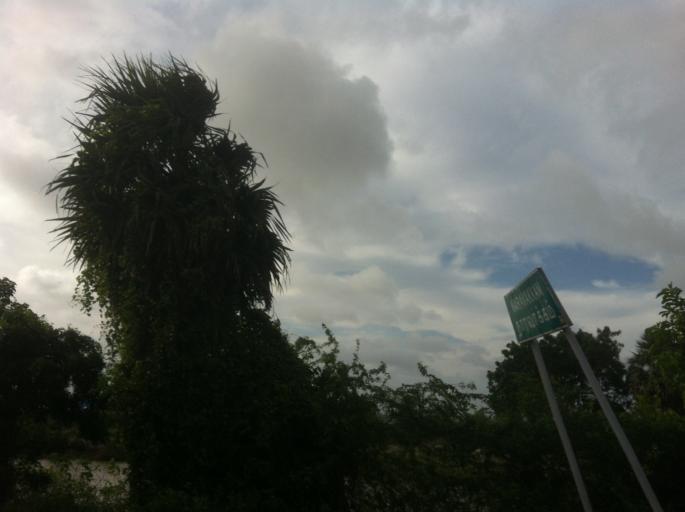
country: IN
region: Tamil Nadu
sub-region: Villupuram
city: Marakkanam
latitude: 12.2062
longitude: 79.9665
